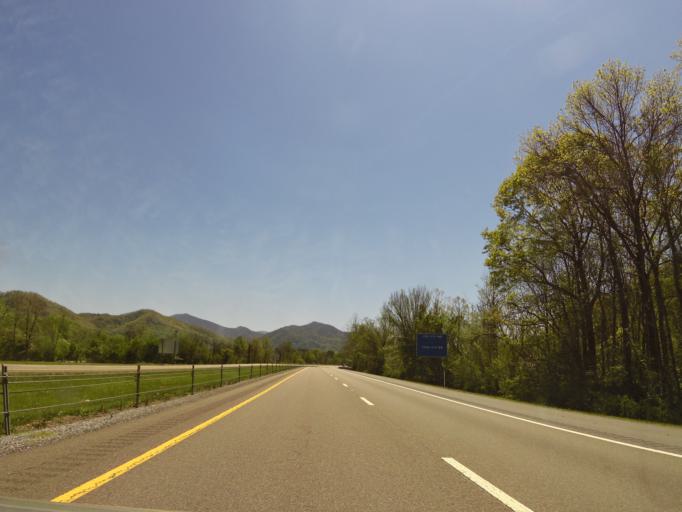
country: US
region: Tennessee
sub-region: Unicoi County
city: Banner Hill
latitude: 36.1391
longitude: -82.4303
